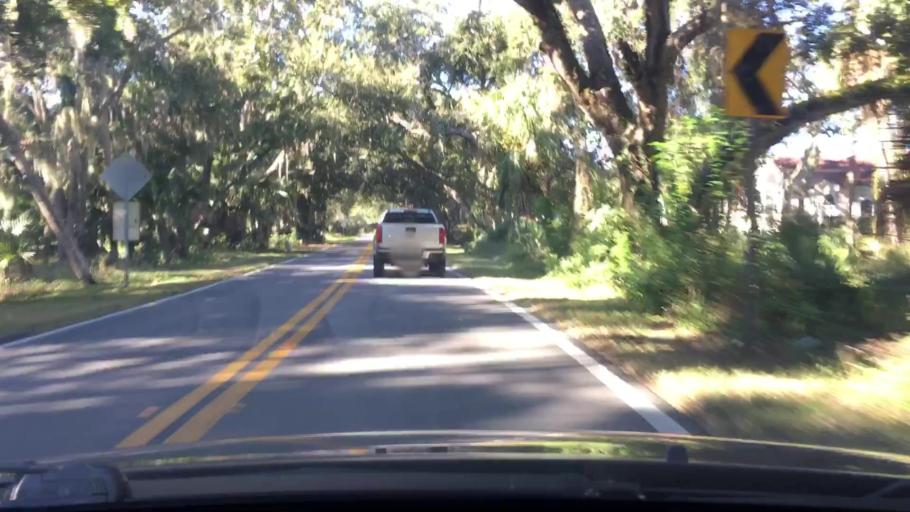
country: US
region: Florida
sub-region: Volusia County
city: Ormond-by-the-Sea
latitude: 29.3473
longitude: -81.0950
